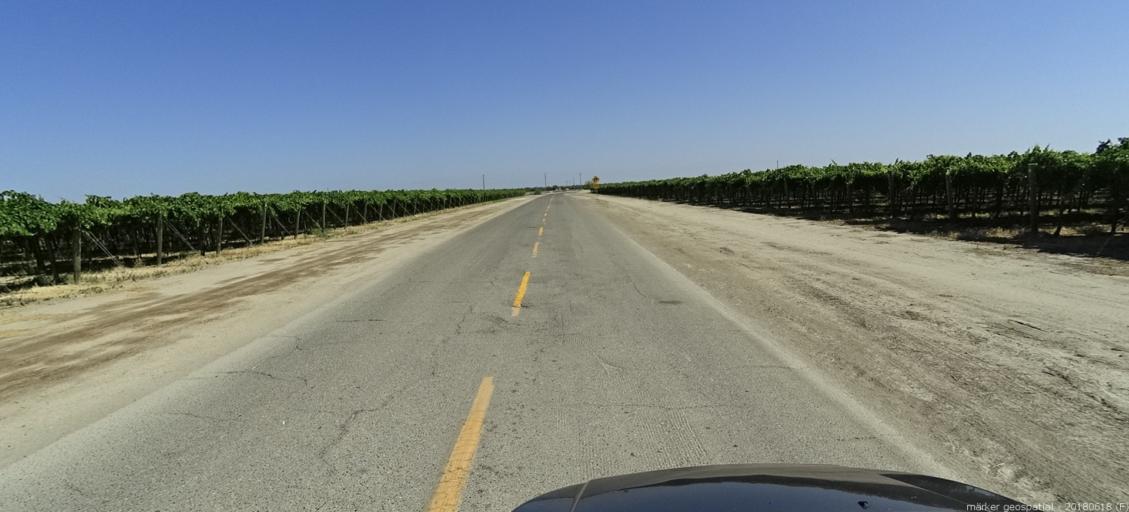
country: US
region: California
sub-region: Fresno County
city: Mendota
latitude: 36.8341
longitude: -120.2591
